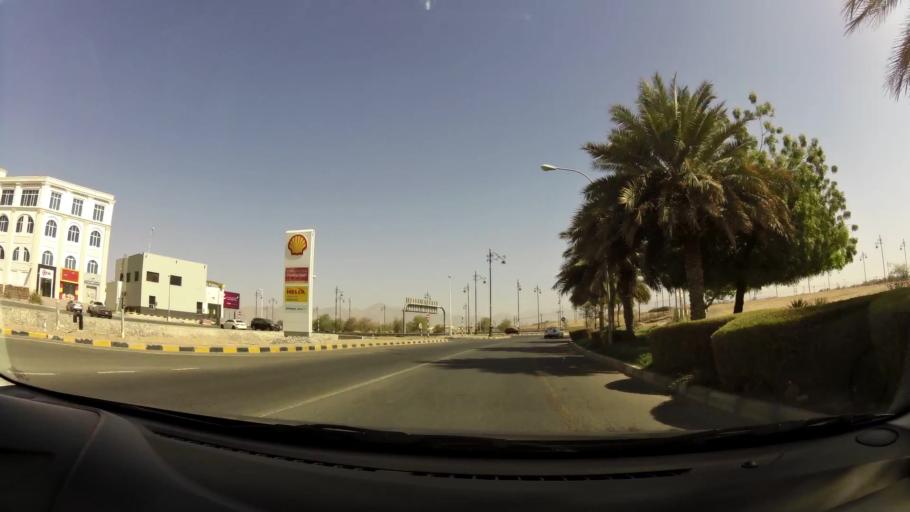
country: OM
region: Muhafazat Masqat
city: Bawshar
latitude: 23.5932
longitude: 58.3487
